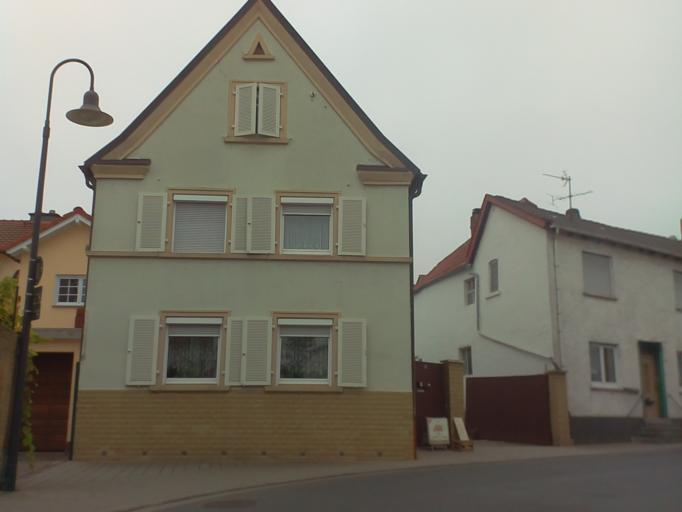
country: DE
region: Rheinland-Pfalz
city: Ellerstadt
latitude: 49.4627
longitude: 8.2625
